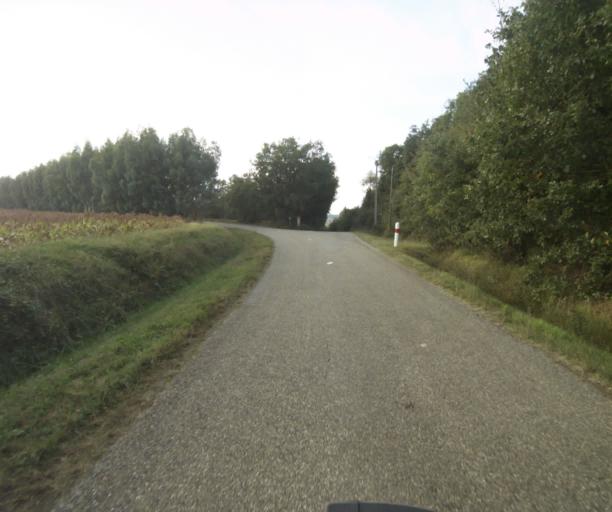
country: FR
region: Midi-Pyrenees
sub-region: Departement de la Haute-Garonne
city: Launac
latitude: 43.8146
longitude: 1.0955
